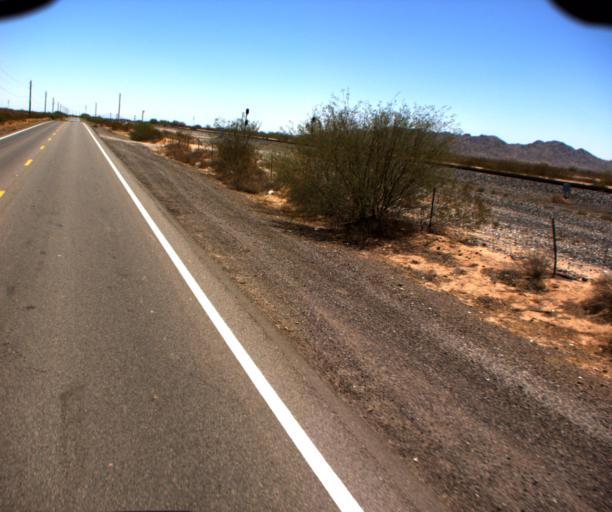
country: US
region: Arizona
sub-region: Pinal County
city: Maricopa
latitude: 33.0669
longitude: -112.2266
